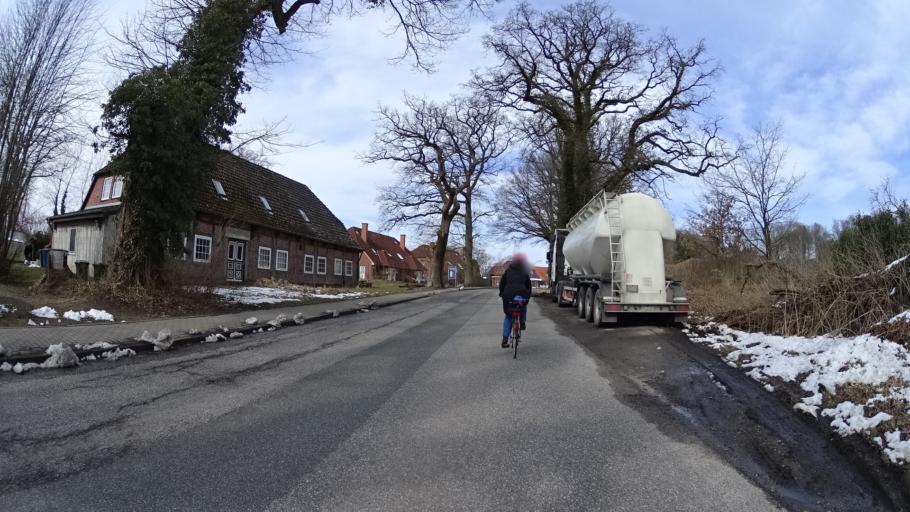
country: DE
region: Schleswig-Holstein
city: Kuhren
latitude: 54.2027
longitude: 10.2608
